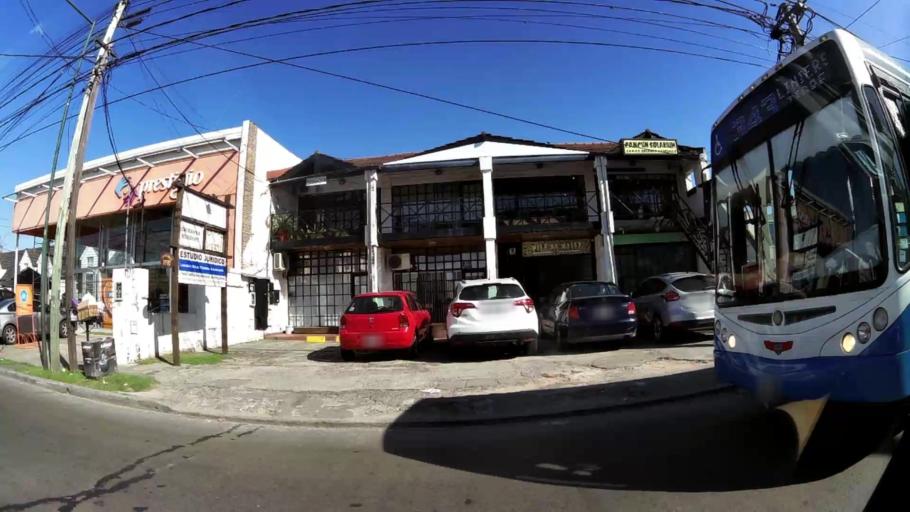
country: AR
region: Buenos Aires
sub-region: Partido de San Isidro
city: San Isidro
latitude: -34.4808
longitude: -58.5546
